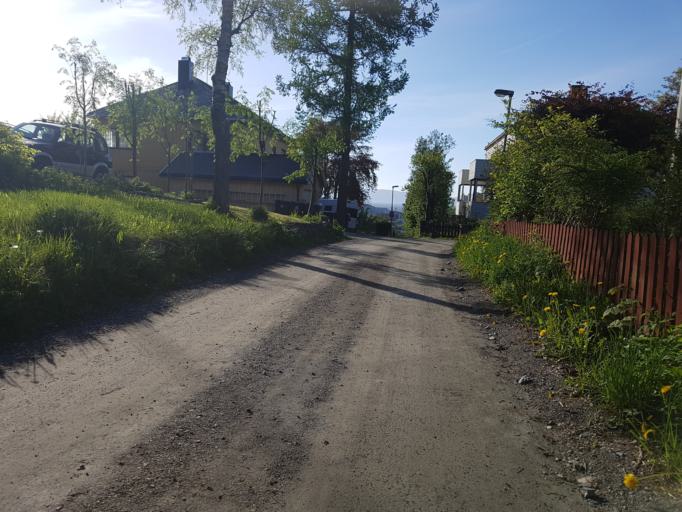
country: NO
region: Sor-Trondelag
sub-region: Trondheim
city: Trondheim
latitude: 63.4324
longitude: 10.4215
